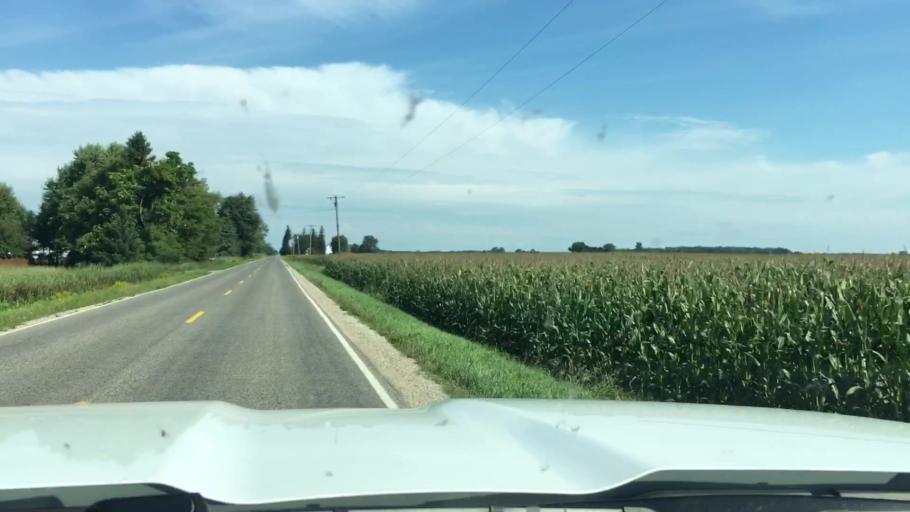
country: US
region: Michigan
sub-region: Saginaw County
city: Hemlock
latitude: 43.5130
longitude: -84.2295
